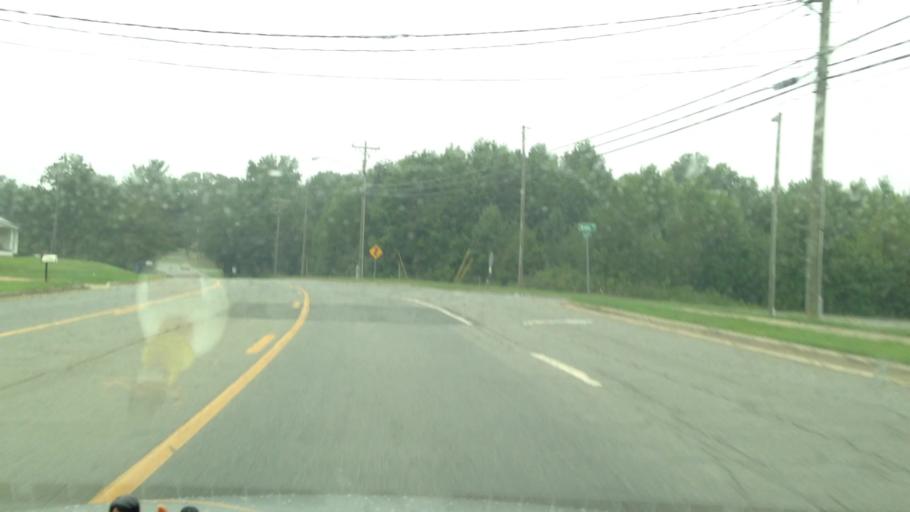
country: US
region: North Carolina
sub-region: Forsyth County
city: Kernersville
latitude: 36.1352
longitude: -80.0712
